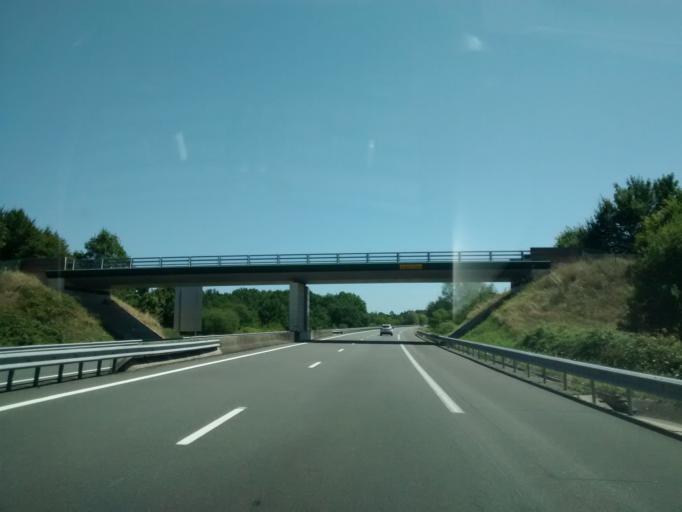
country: FR
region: Aquitaine
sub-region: Departement de la Gironde
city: Saint-Medard-de-Guizieres
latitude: 45.0077
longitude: -0.0356
